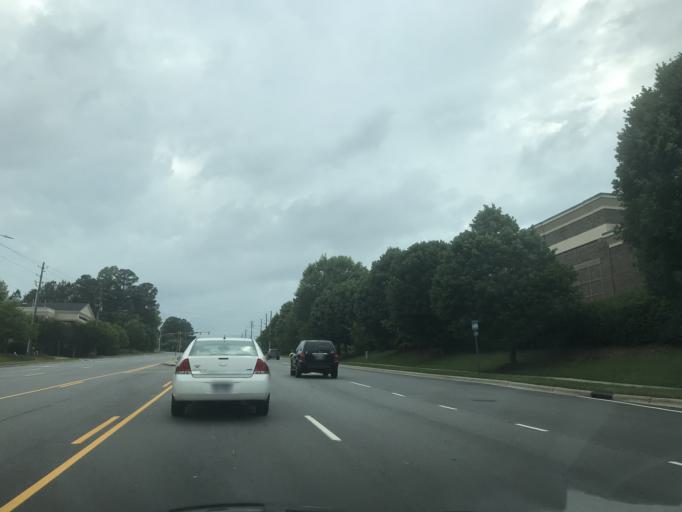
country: US
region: North Carolina
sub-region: Wake County
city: Cary
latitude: 35.8029
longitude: -78.7804
